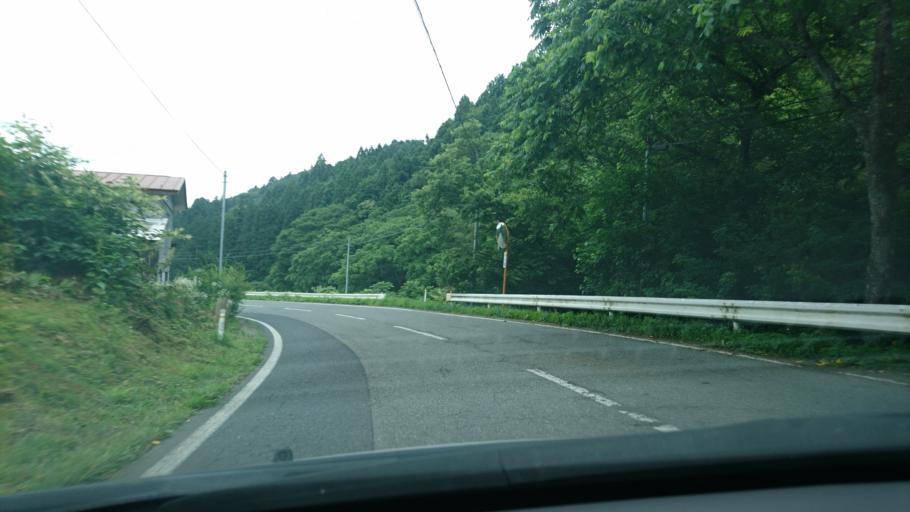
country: JP
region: Iwate
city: Ichinoseki
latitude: 38.8694
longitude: 141.4247
